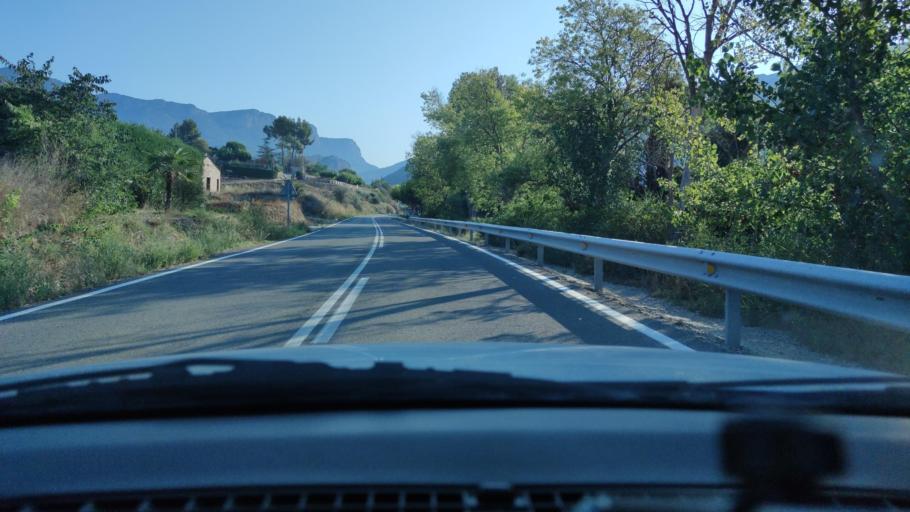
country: ES
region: Catalonia
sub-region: Provincia de Lleida
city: Camarasa
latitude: 41.8628
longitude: 0.8373
